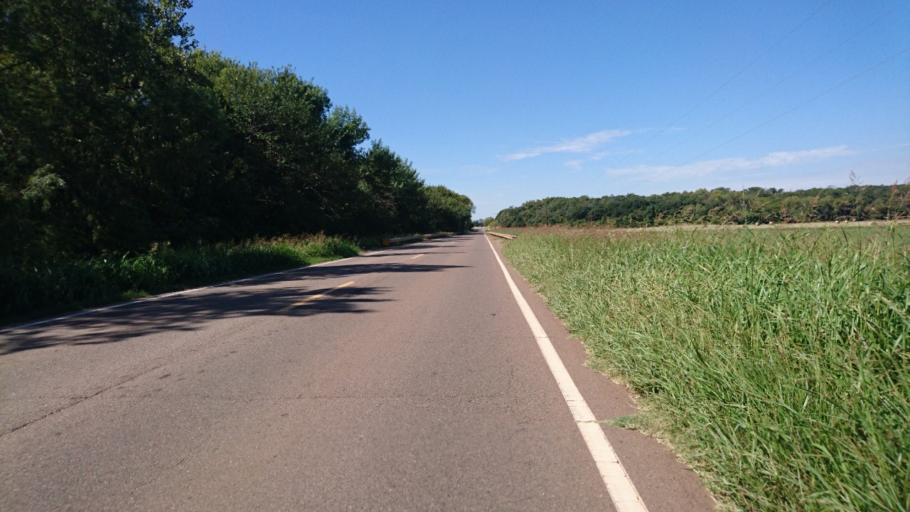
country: US
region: Oklahoma
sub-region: Oklahoma County
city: Luther
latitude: 35.6606
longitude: -97.2695
